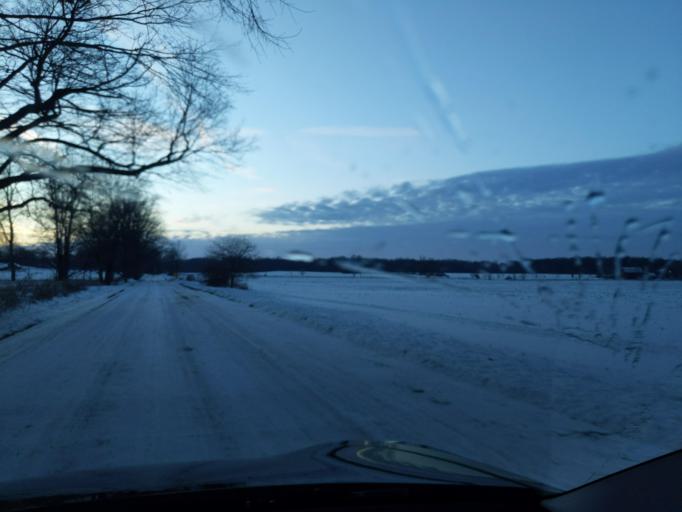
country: US
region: Michigan
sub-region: Ingham County
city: Mason
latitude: 42.5704
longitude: -84.3526
